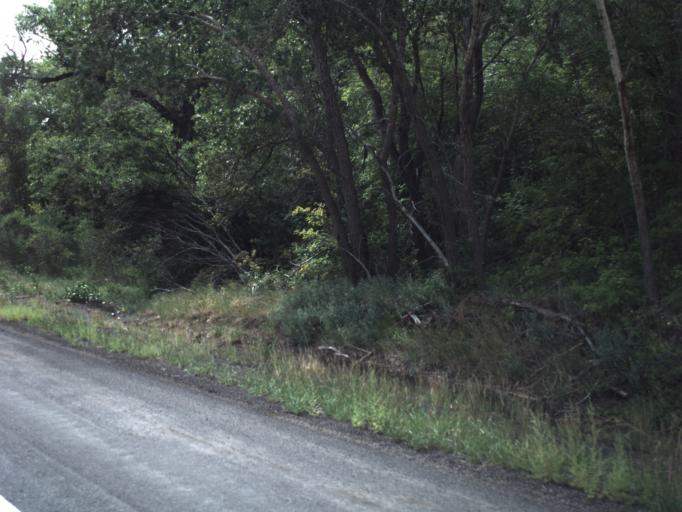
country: US
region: Utah
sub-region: Carbon County
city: Helper
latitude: 39.7630
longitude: -110.8963
